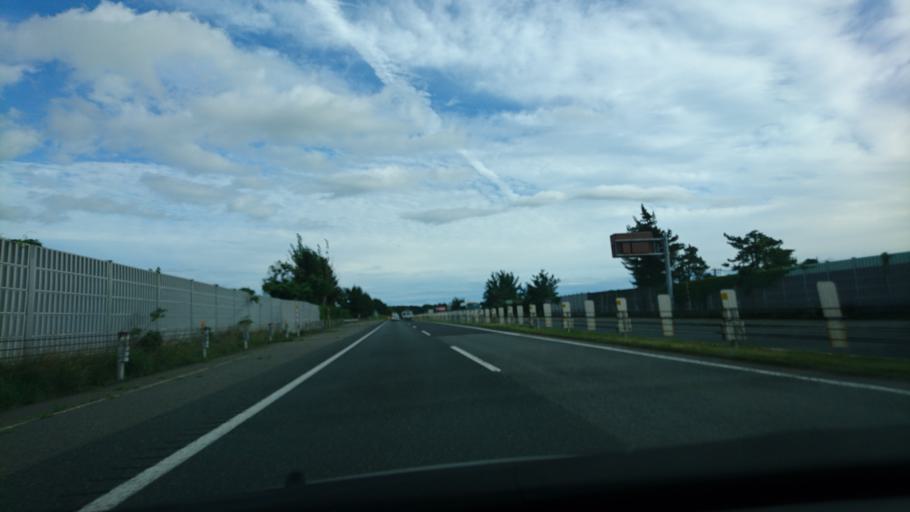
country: JP
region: Iwate
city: Hanamaki
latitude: 39.3821
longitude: 141.0916
